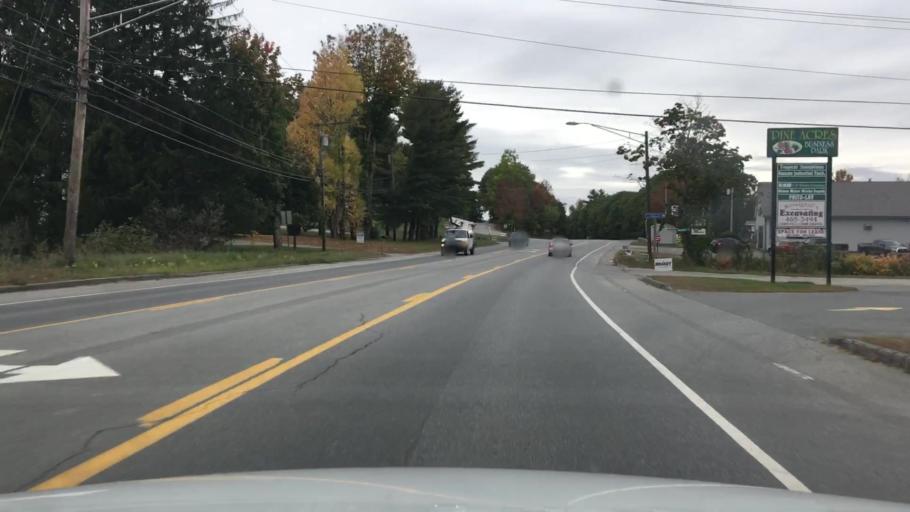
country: US
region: Maine
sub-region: Kennebec County
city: Oakland
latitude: 44.5443
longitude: -69.6937
